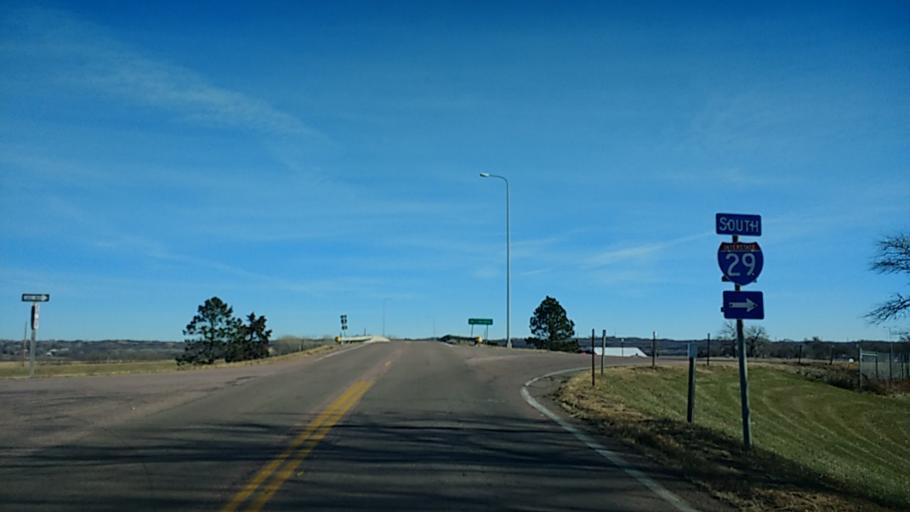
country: US
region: South Dakota
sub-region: Union County
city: North Sioux City
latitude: 42.5502
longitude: -96.5104
